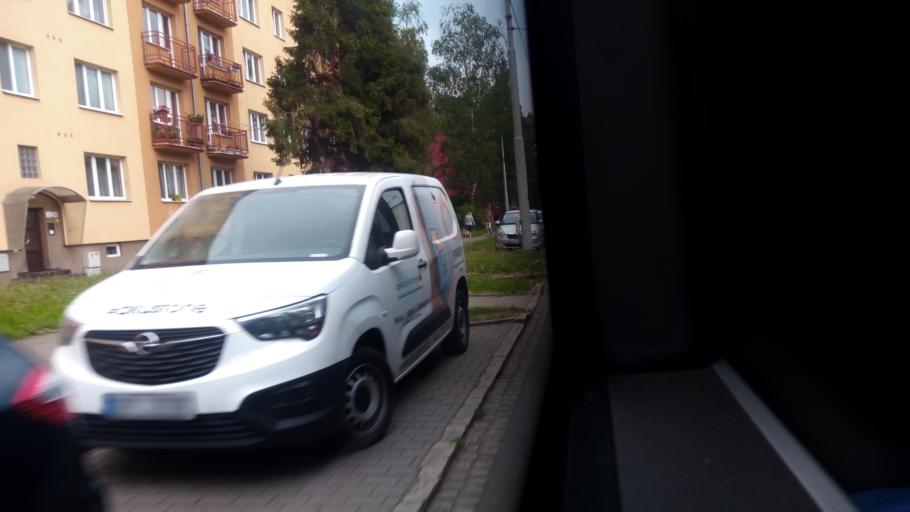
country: CZ
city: Vresina
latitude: 49.8342
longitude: 18.1765
